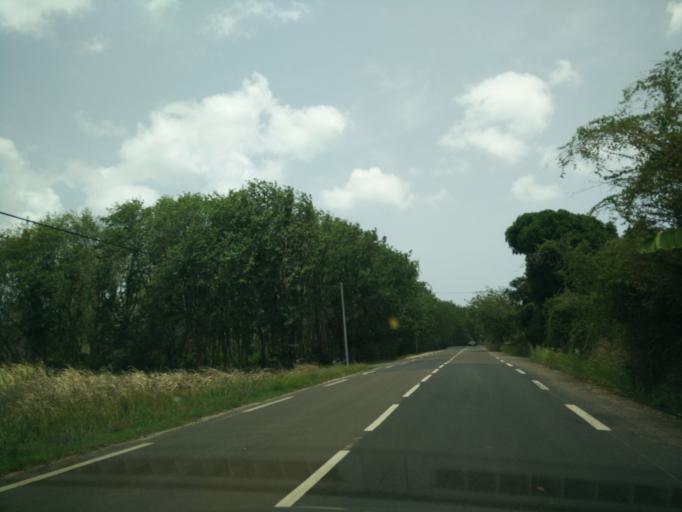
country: GP
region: Guadeloupe
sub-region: Guadeloupe
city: Anse-Bertrand
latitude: 16.4593
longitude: -61.5115
